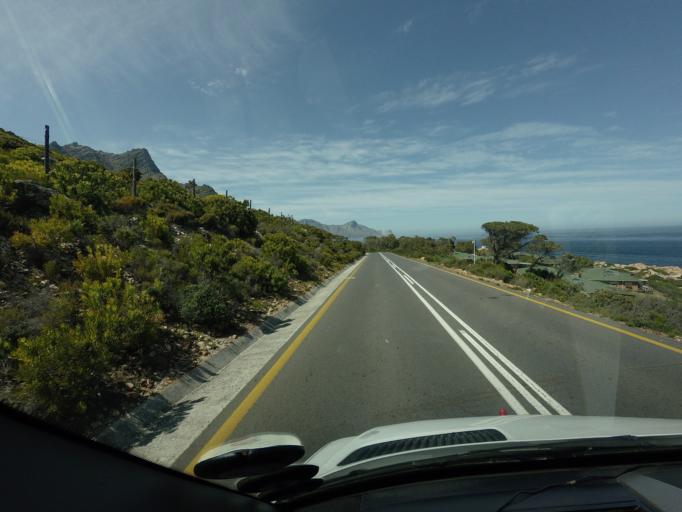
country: ZA
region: Western Cape
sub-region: Overberg District Municipality
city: Grabouw
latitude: -34.1890
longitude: 18.8199
